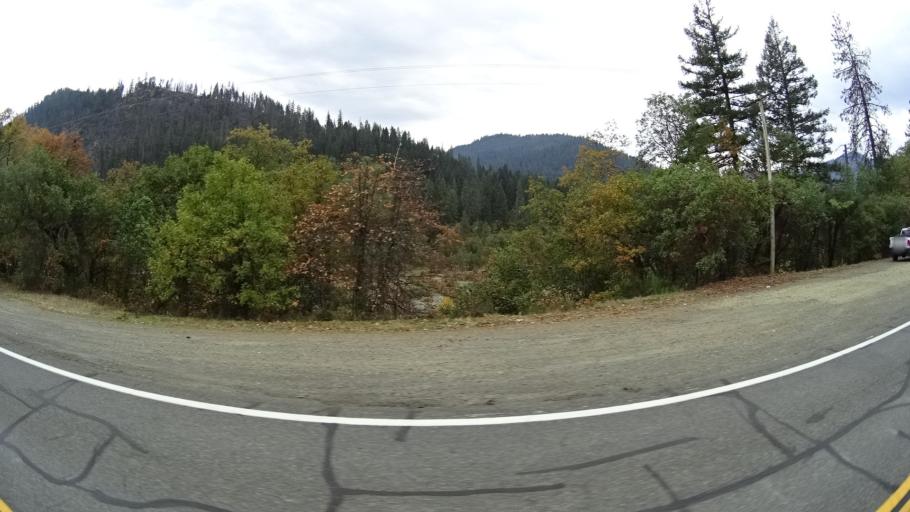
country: US
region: California
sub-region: Siskiyou County
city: Happy Camp
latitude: 41.7878
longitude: -123.3907
